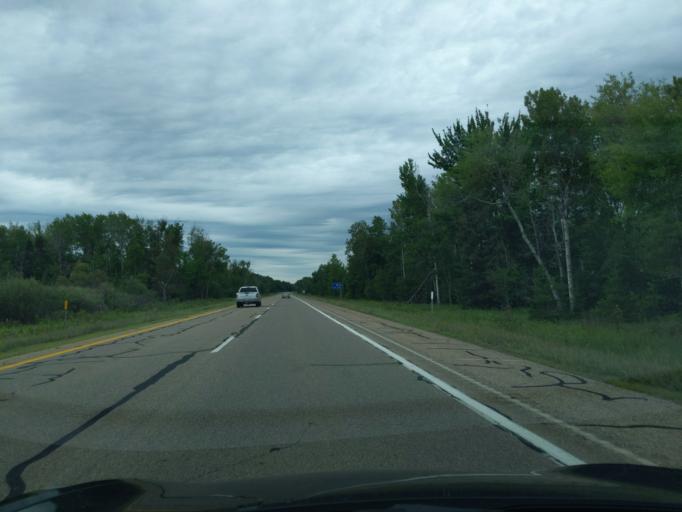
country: US
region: Michigan
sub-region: Roscommon County
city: Houghton Lake
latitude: 44.2855
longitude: -84.8008
